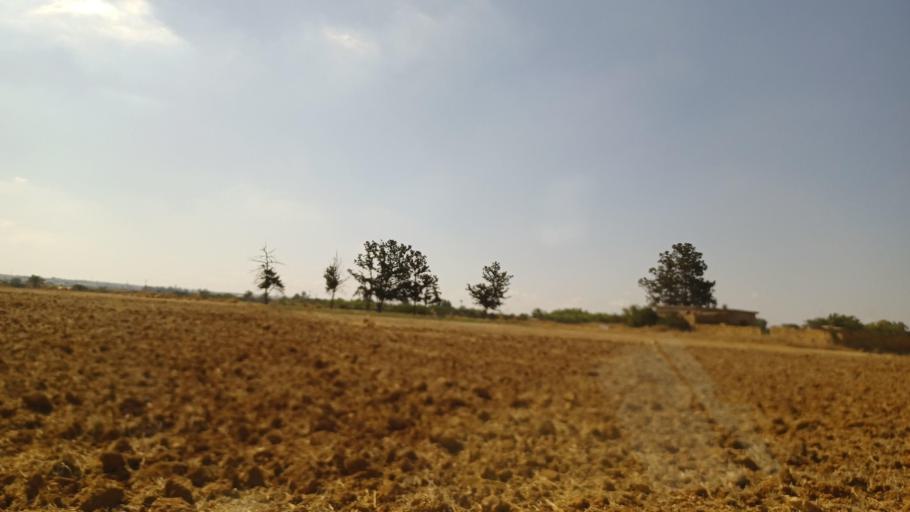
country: CY
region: Ammochostos
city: Acheritou
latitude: 35.0680
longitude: 33.8648
